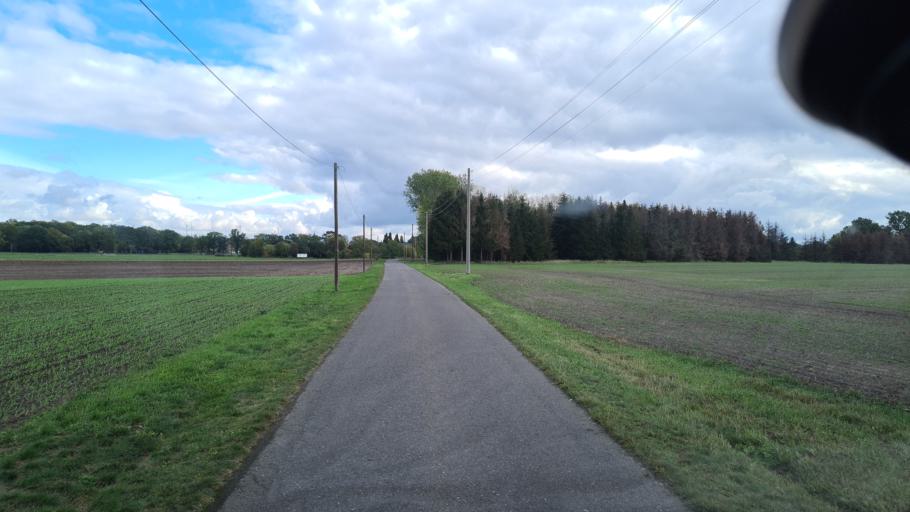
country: DE
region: Brandenburg
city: Sallgast
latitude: 51.6066
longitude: 13.8933
